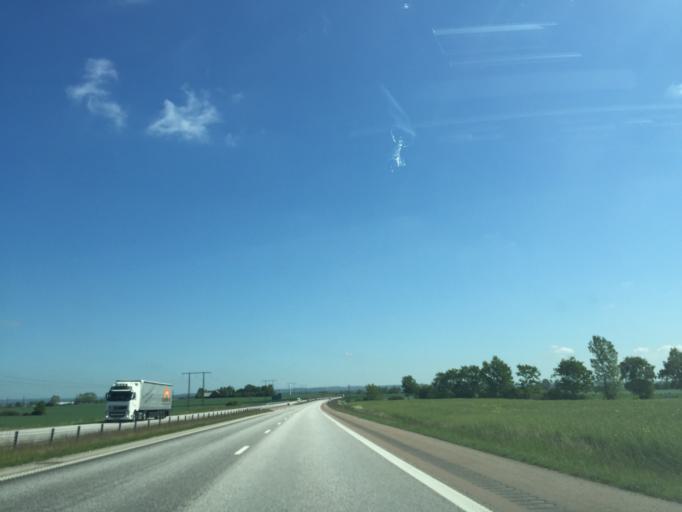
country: SE
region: Skane
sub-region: Astorps Kommun
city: Astorp
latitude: 56.1528
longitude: 12.9470
